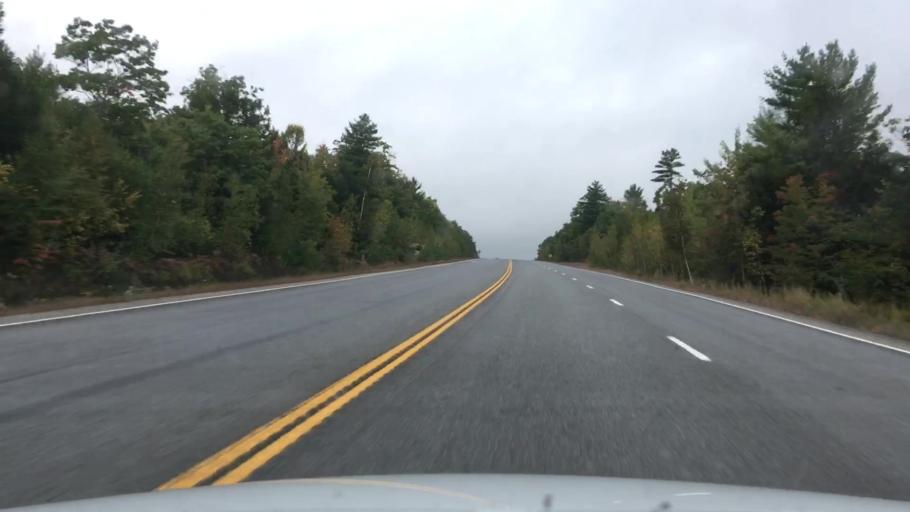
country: US
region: Maine
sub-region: Cumberland County
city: New Gloucester
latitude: 43.9569
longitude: -70.3532
